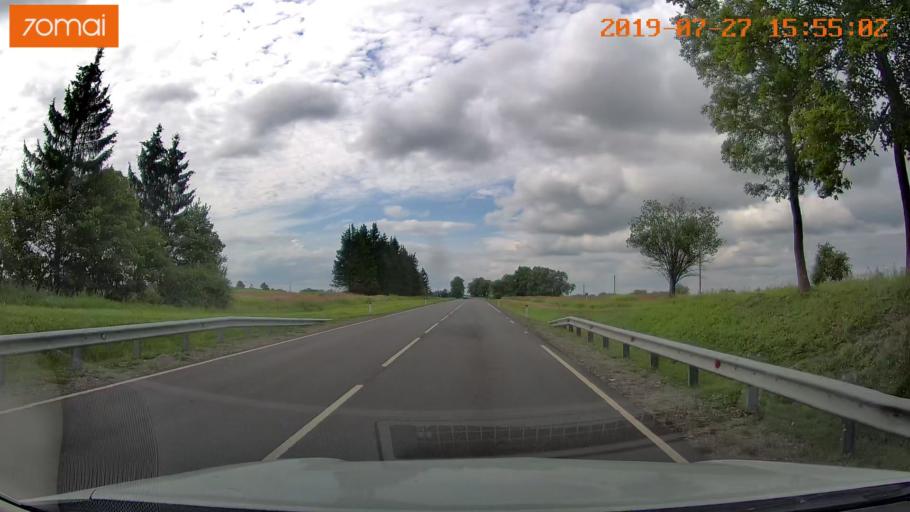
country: RU
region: Kaliningrad
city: Chernyakhovsk
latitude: 54.6112
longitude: 21.9280
